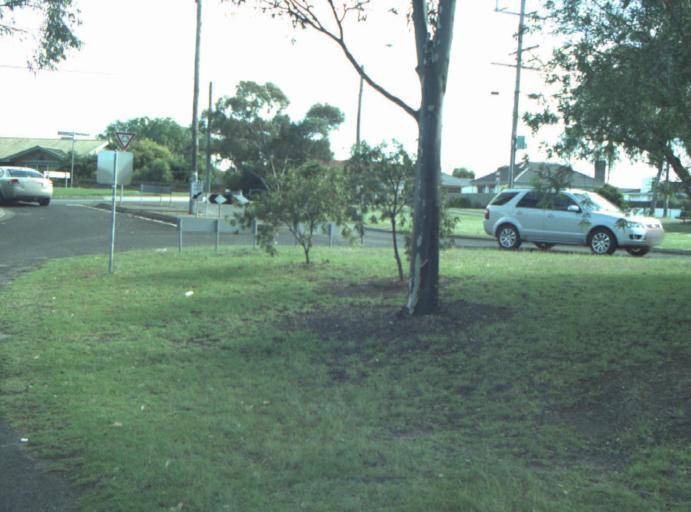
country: AU
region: Victoria
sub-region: Greater Geelong
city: Lara
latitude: -38.0214
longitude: 144.4063
